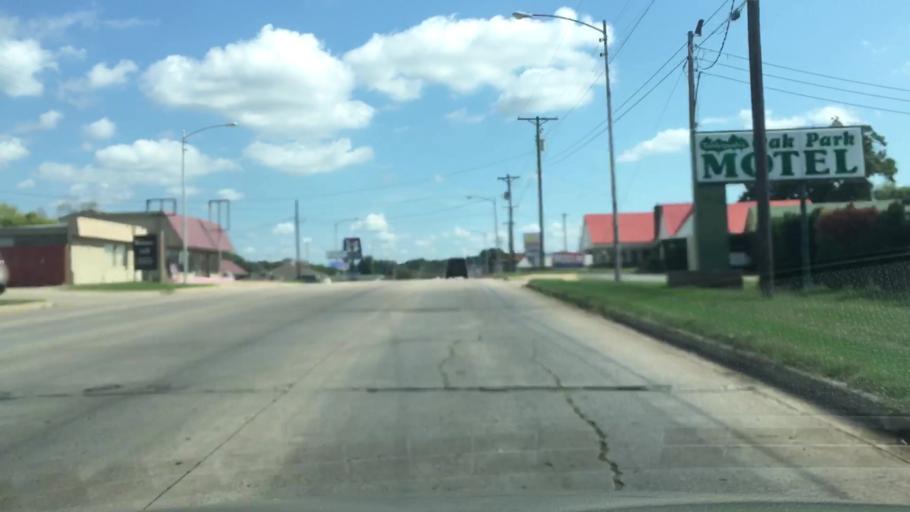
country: US
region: Oklahoma
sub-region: Cherokee County
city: Tahlequah
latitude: 35.9153
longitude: -94.9611
